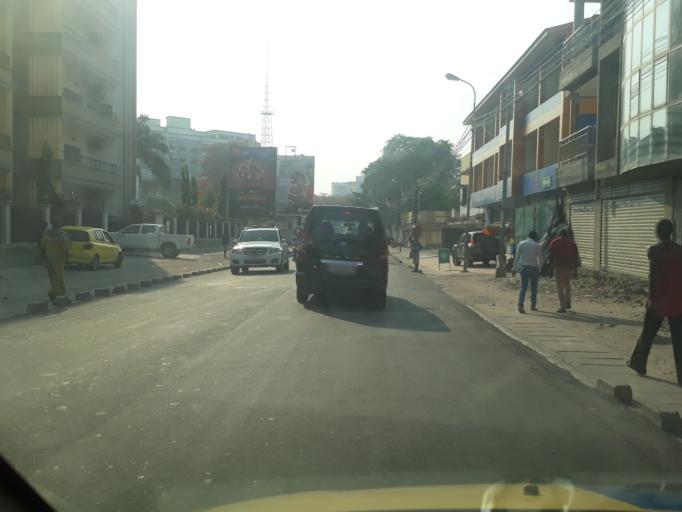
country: CD
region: Kinshasa
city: Kinshasa
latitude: -4.3054
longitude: 15.3216
